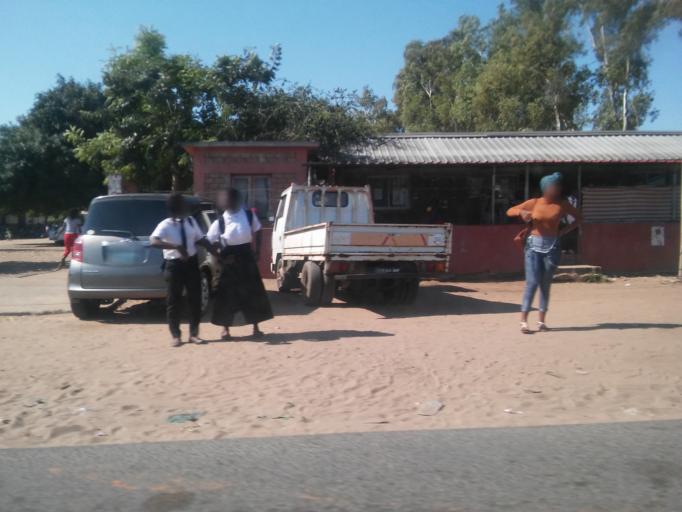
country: MZ
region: Maputo City
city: Maputo
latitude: -25.8588
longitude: 32.5670
